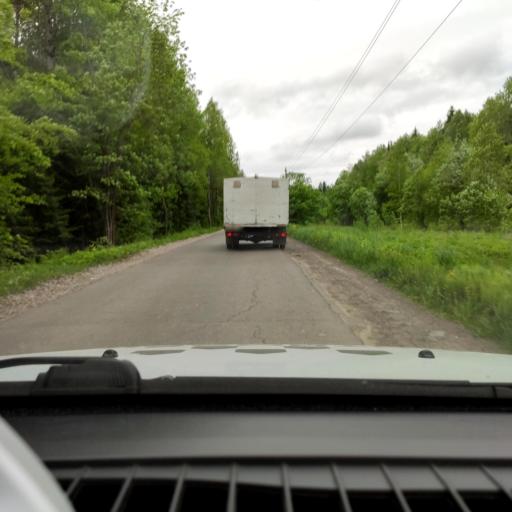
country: RU
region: Perm
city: Novyye Lyady
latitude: 58.0415
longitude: 56.6294
